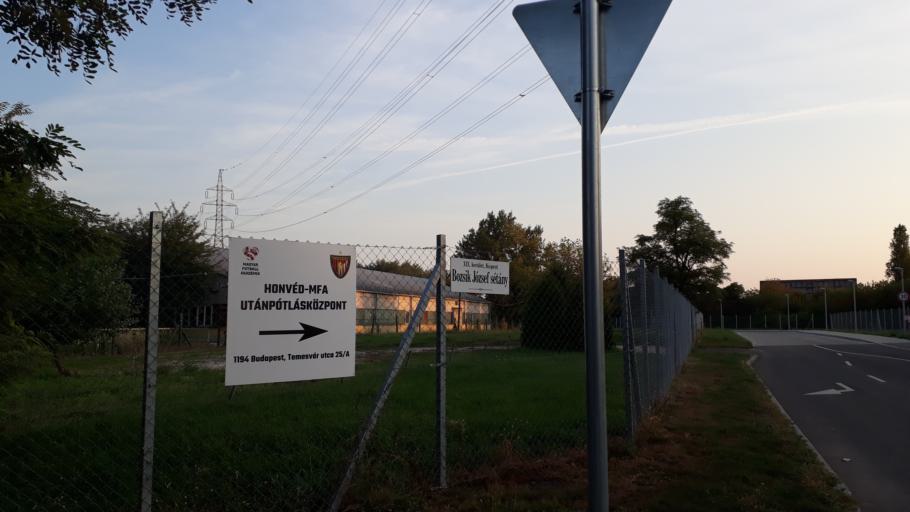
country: HU
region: Budapest
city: Budapest XIX. keruelet
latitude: 47.4358
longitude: 19.1525
